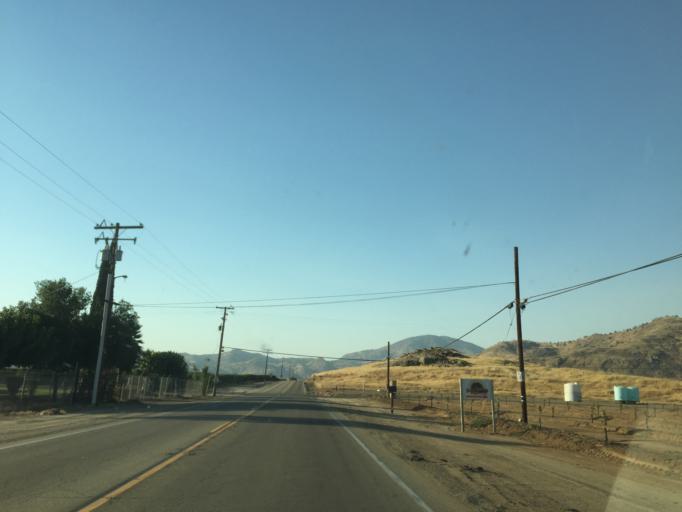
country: US
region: California
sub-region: Fresno County
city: Orange Cove
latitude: 36.6596
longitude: -119.3046
